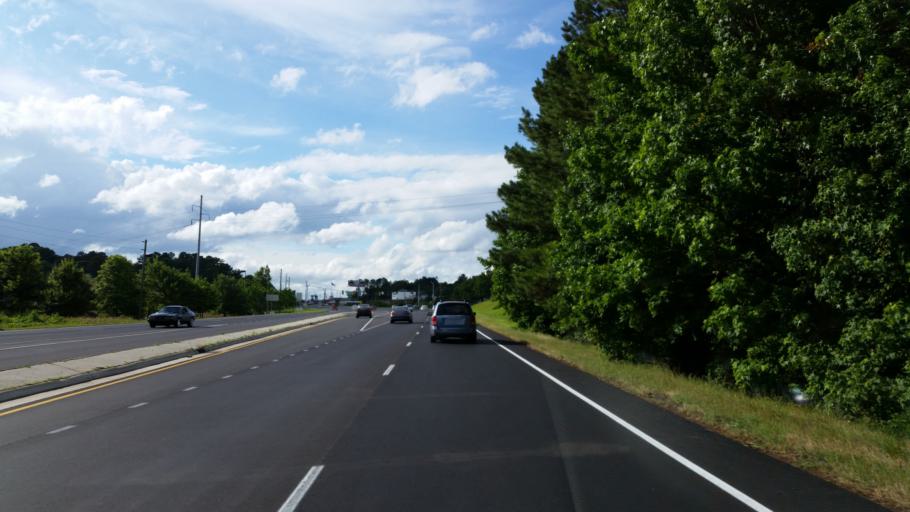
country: US
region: Georgia
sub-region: Bartow County
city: Cartersville
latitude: 34.1847
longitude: -84.7857
